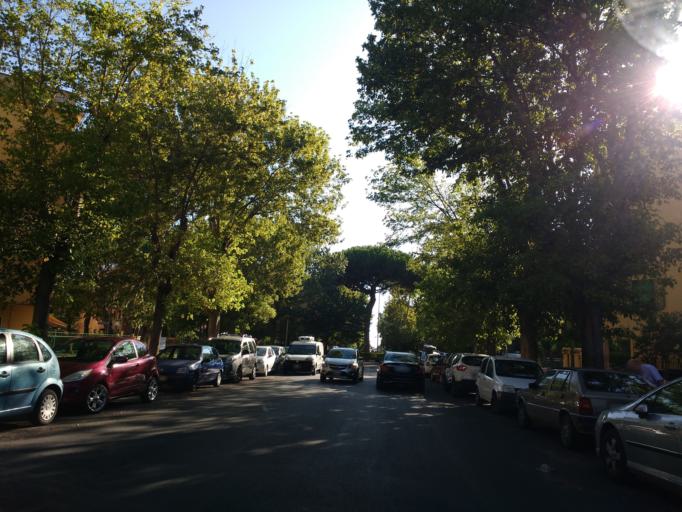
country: IT
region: Latium
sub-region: Citta metropolitana di Roma Capitale
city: Acilia-Castel Fusano-Ostia Antica
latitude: 41.7781
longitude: 12.3561
